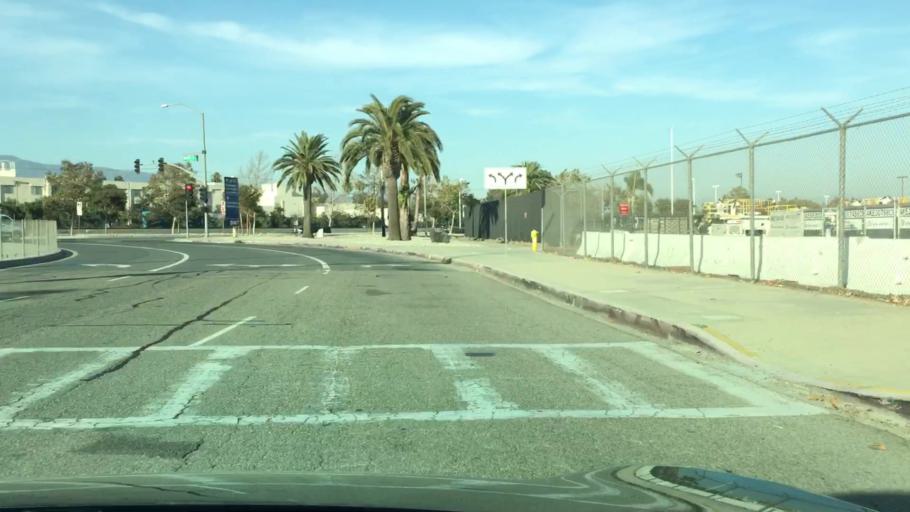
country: US
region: California
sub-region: San Bernardino County
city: Ontario
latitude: 34.0616
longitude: -117.6068
